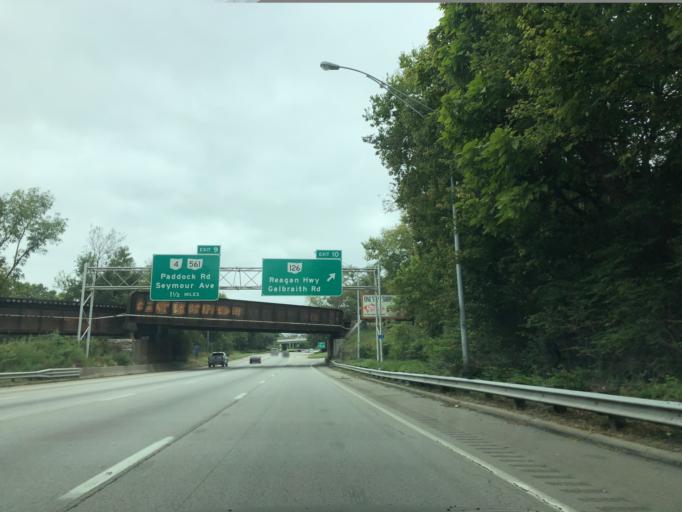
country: US
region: Ohio
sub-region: Hamilton County
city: Lockland
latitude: 39.2149
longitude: -84.4610
